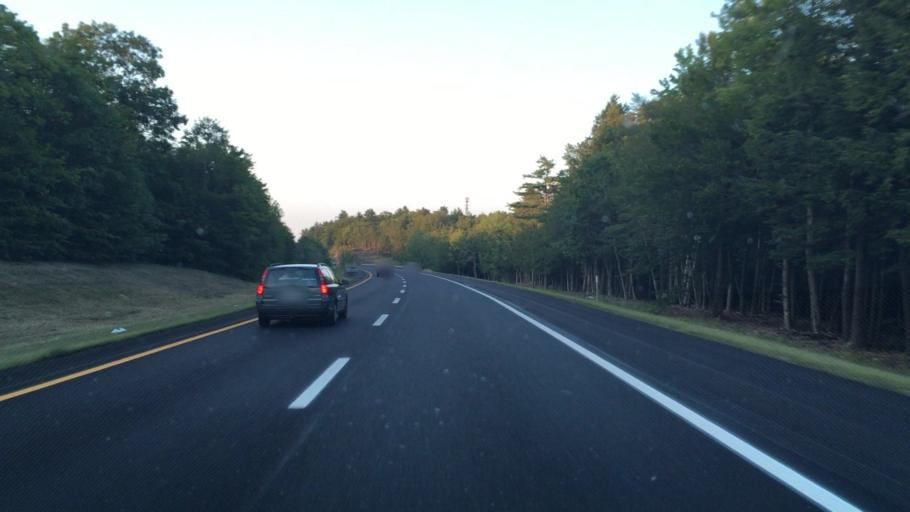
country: US
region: Maine
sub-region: Sagadahoc County
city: Topsham
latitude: 43.9726
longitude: -69.9476
